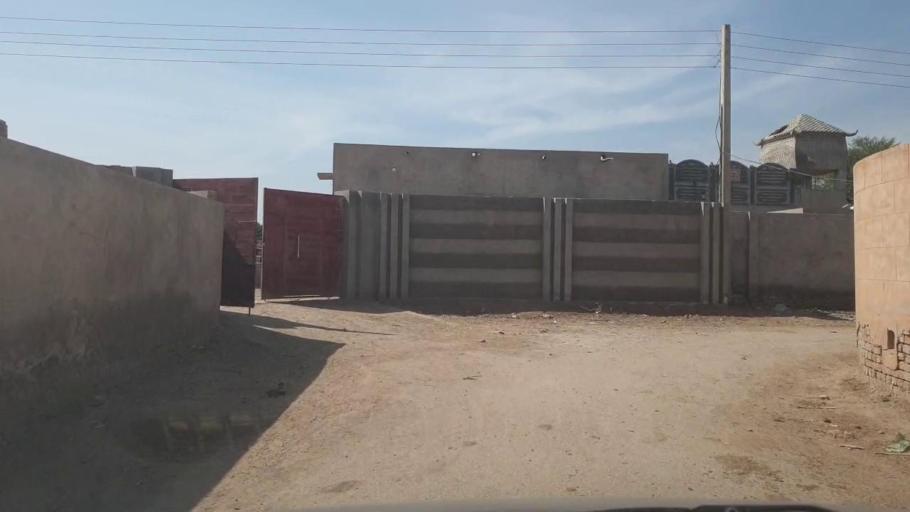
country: PK
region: Sindh
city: Kunri
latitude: 25.1867
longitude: 69.6742
